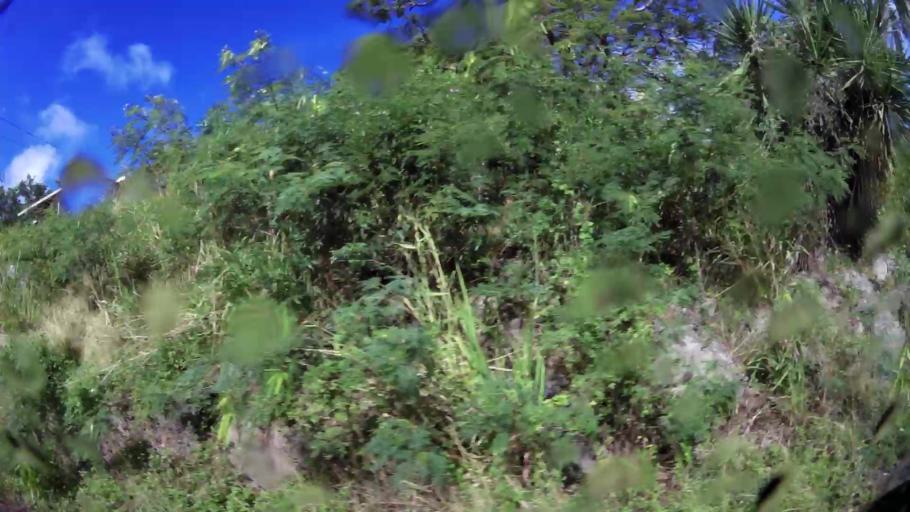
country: MS
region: Saint Peter
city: Saint Peters
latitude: 16.7448
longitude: -62.2273
